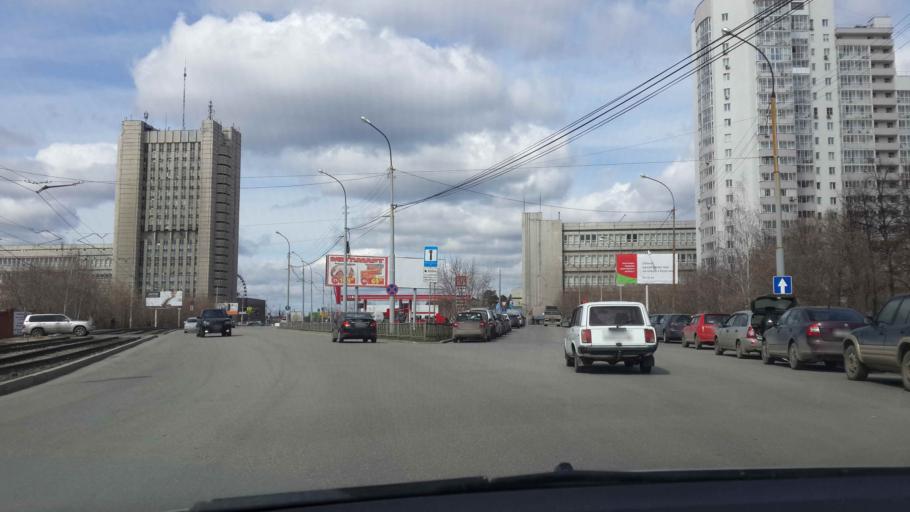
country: RU
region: Sverdlovsk
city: Sovkhoznyy
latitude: 56.8133
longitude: 60.5552
